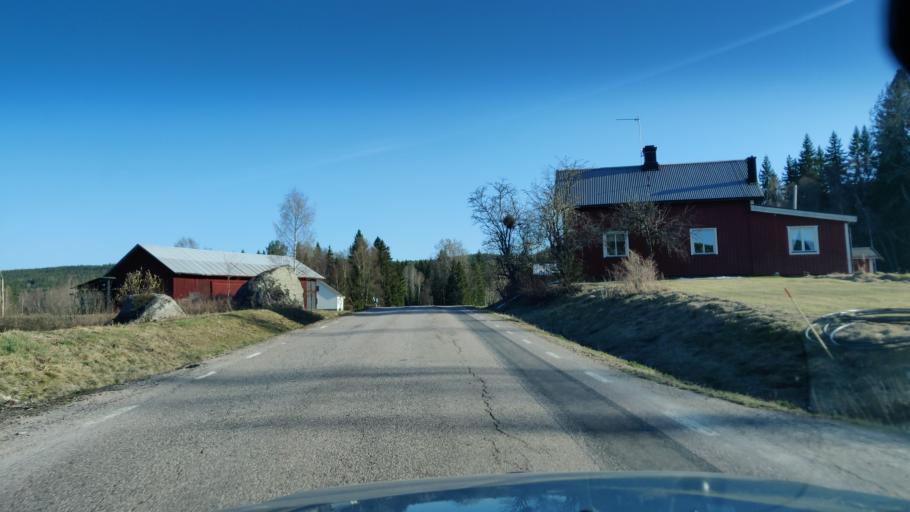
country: SE
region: Vaermland
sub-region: Munkfors Kommun
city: Munkfors
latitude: 59.9765
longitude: 13.4131
